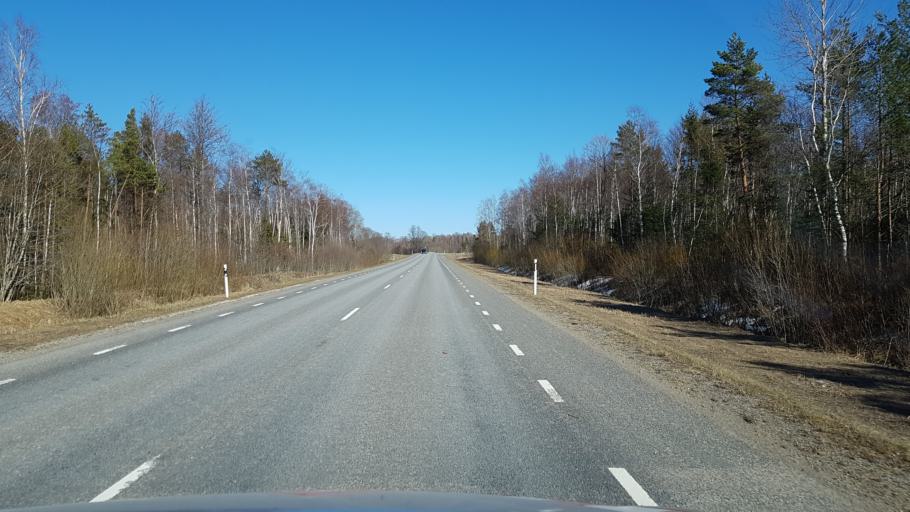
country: EE
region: Ida-Virumaa
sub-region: Aseri vald
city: Aseri
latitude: 59.3551
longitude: 26.7177
